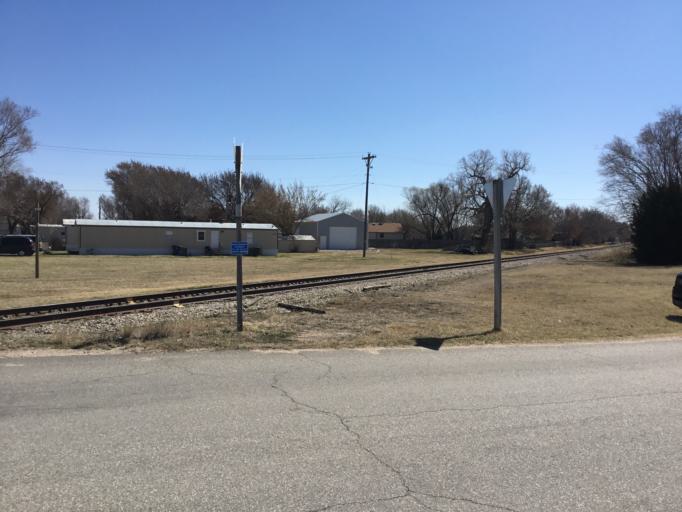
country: US
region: Kansas
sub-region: Sedgwick County
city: Maize
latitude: 37.7801
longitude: -97.4688
